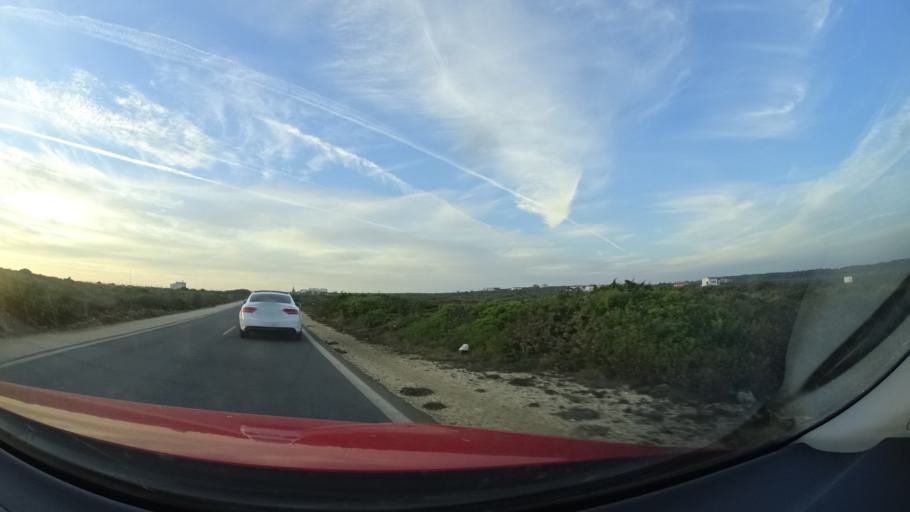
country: PT
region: Faro
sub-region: Vila do Bispo
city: Sagres
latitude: 37.0205
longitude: -8.9586
